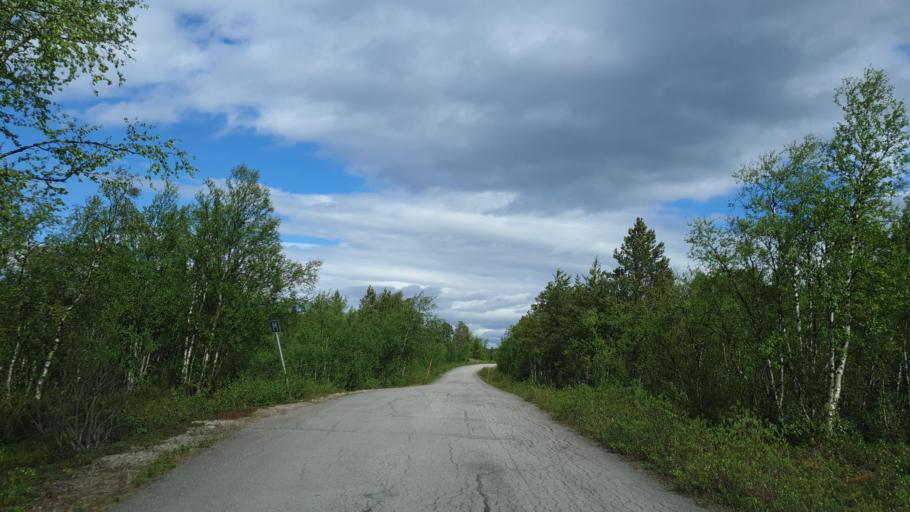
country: SE
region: Norrbotten
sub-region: Kiruna Kommun
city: Kiruna
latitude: 68.2235
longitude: 19.7154
